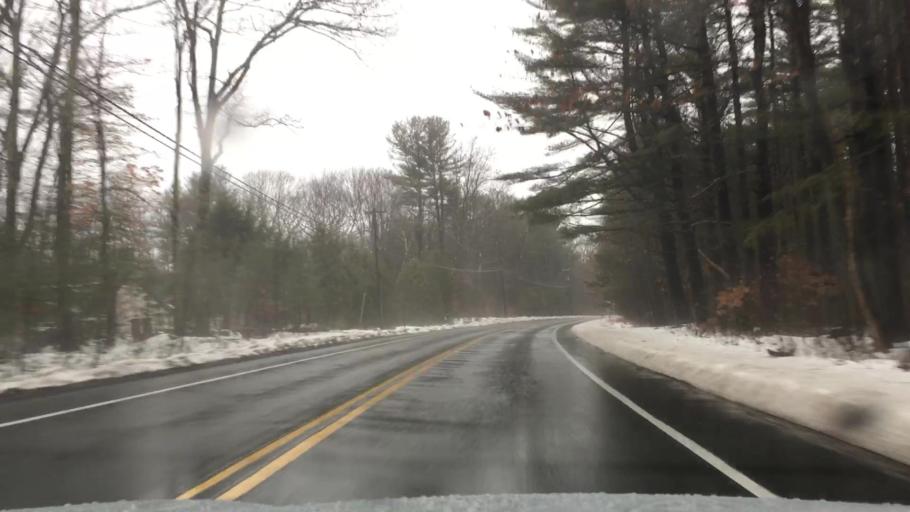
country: US
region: Massachusetts
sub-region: Hampshire County
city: Pelham
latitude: 42.3762
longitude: -72.4007
